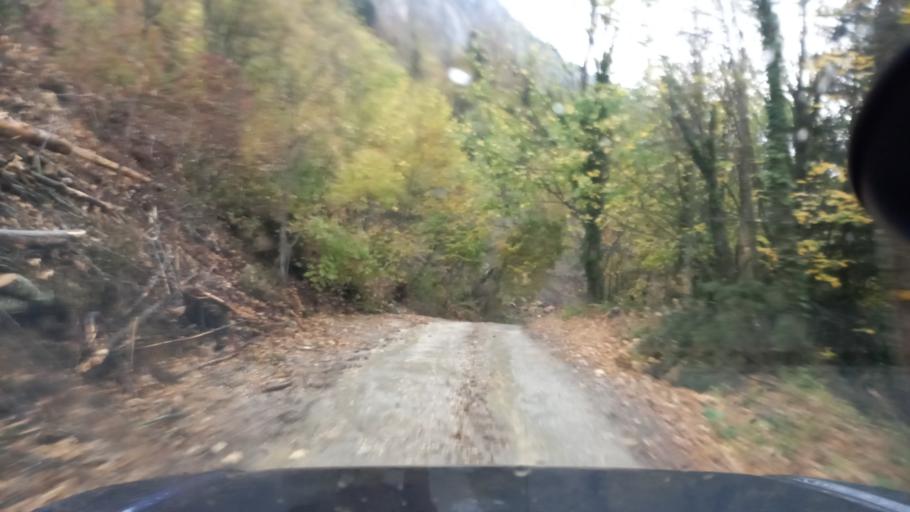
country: RU
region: Krasnodarskiy
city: Neftegorsk
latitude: 44.0478
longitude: 39.8315
